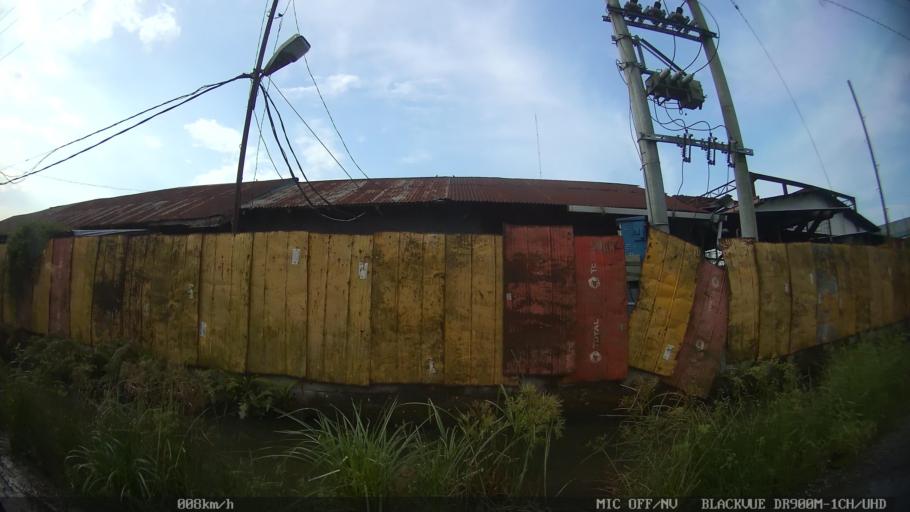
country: ID
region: North Sumatra
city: Medan
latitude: 3.6055
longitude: 98.7359
